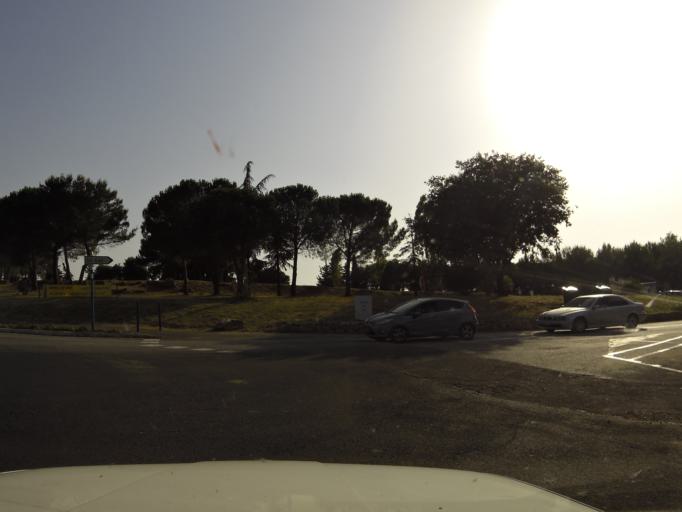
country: FR
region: Languedoc-Roussillon
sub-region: Departement de l'Herault
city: Le Cres
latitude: 43.6559
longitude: 3.9353
